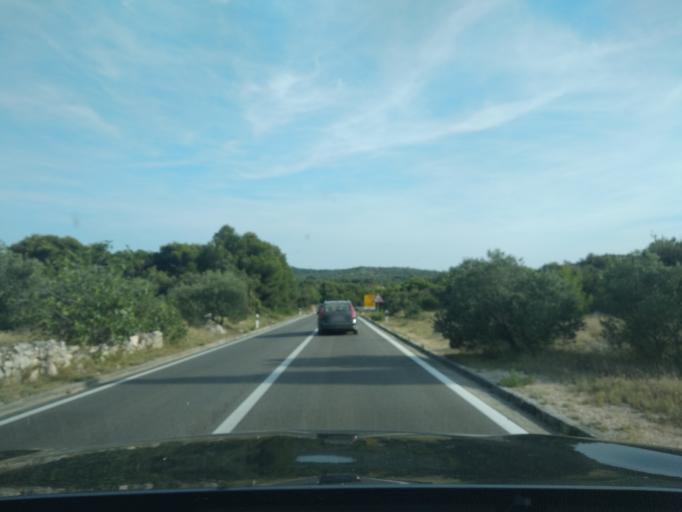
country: HR
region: Sibensko-Kniniska
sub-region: Grad Sibenik
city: Tisno
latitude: 43.7919
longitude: 15.6328
